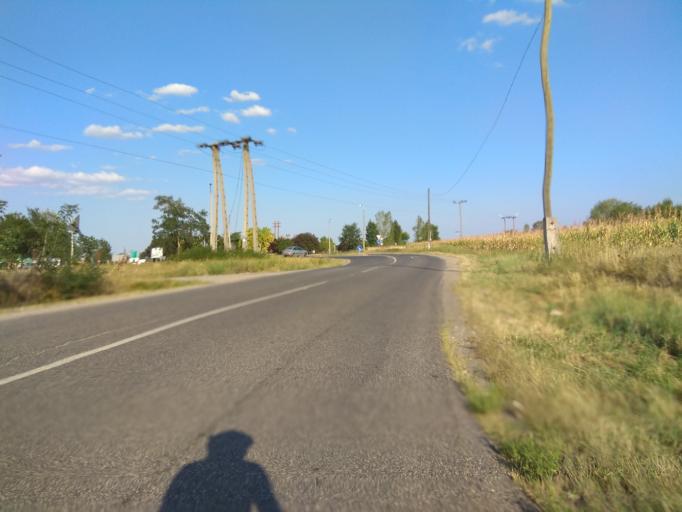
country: HU
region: Borsod-Abauj-Zemplen
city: Onod
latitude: 47.9775
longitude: 20.9103
